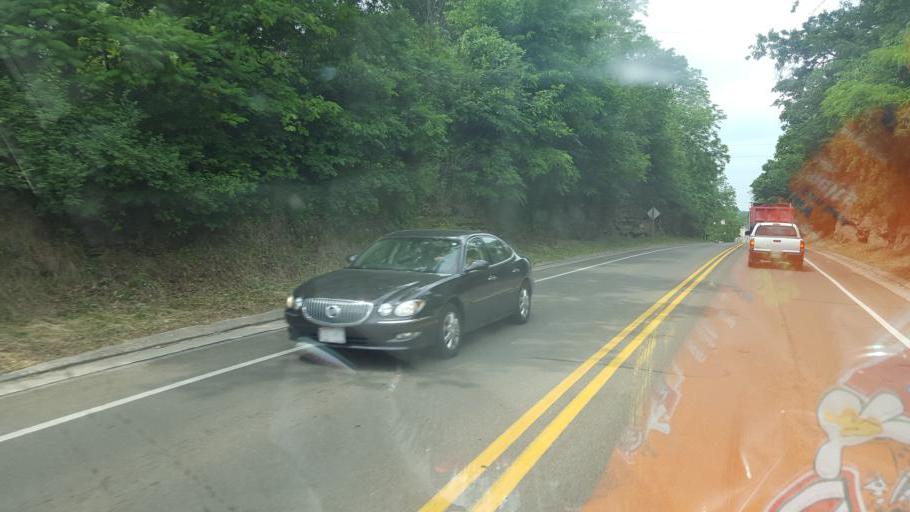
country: US
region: Wisconsin
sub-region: Sauk County
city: Reedsburg
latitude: 43.5816
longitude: -90.1254
